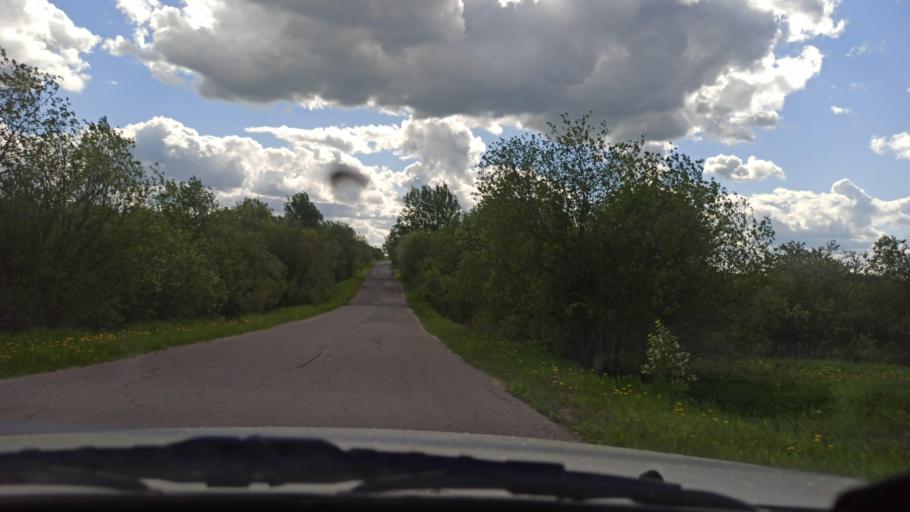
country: RU
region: Vologda
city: Molochnoye
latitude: 59.3764
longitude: 39.7131
